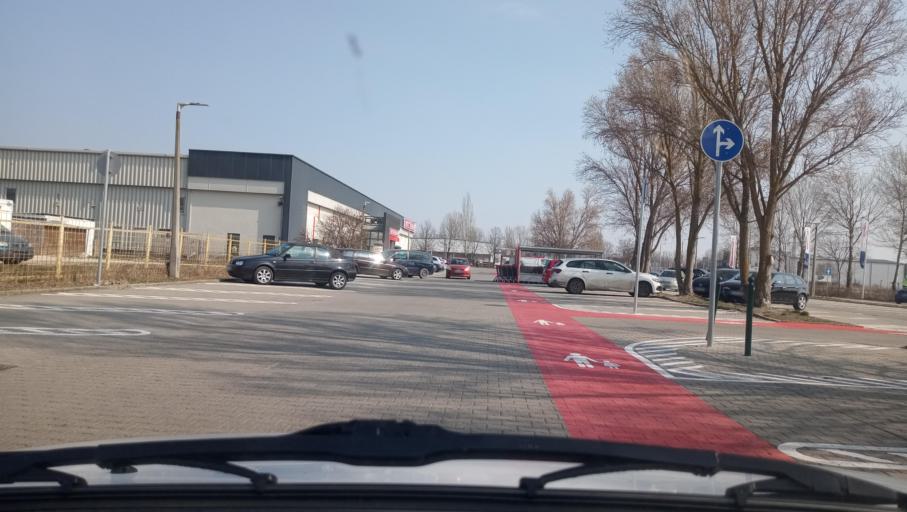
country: HU
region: Pest
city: Szentendre
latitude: 47.6461
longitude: 19.0622
